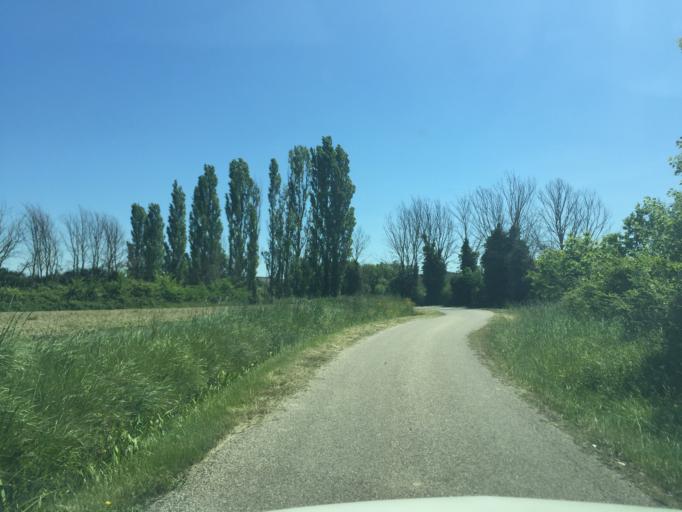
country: FR
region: Provence-Alpes-Cote d'Azur
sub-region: Departement du Vaucluse
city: Caderousse
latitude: 44.0997
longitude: 4.7760
